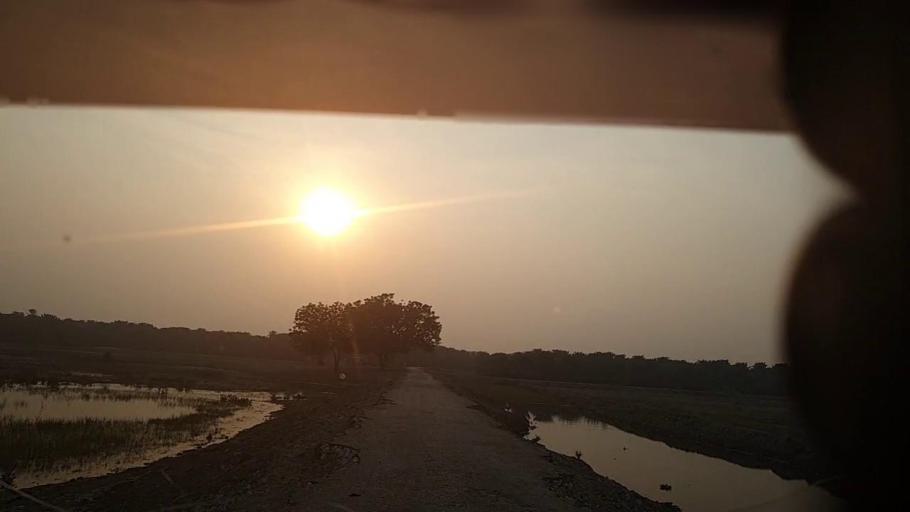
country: PK
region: Sindh
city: Pir jo Goth
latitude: 27.5221
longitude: 68.6532
